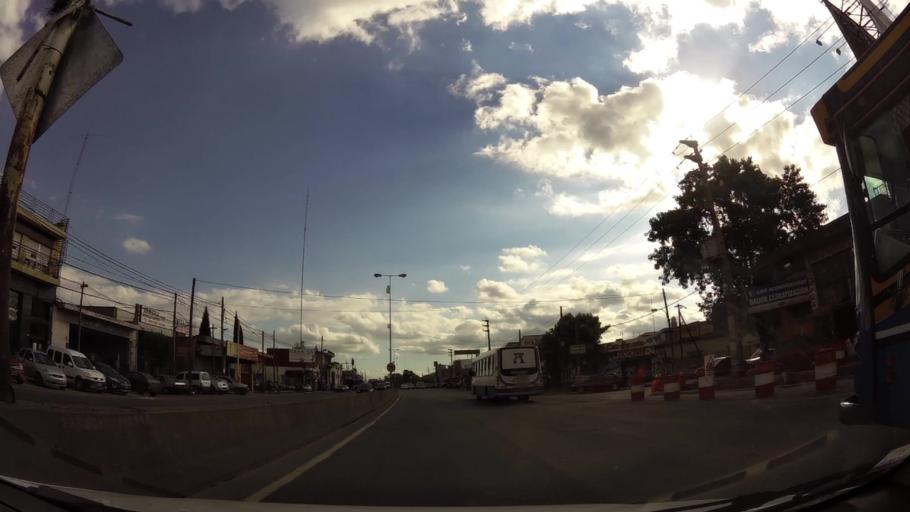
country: AR
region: Buenos Aires
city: San Justo
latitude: -34.6917
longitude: -58.5712
